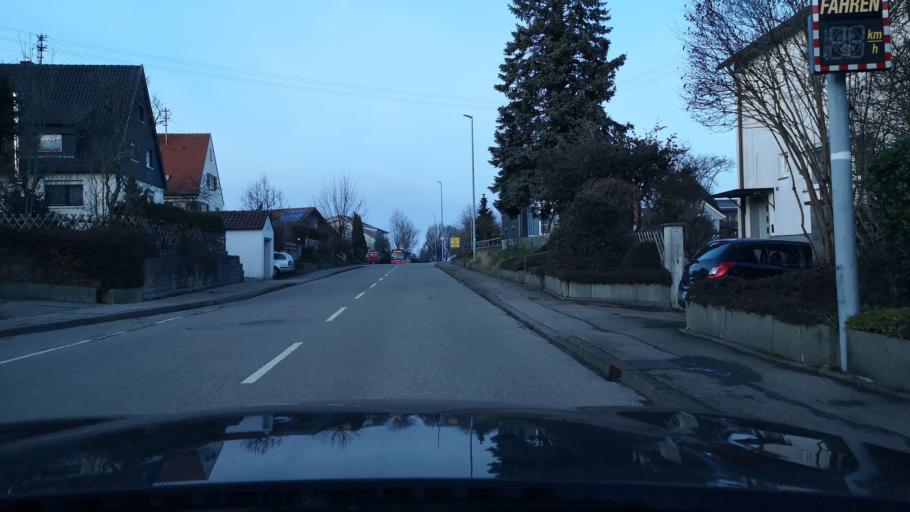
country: DE
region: Baden-Wuerttemberg
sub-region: Regierungsbezirk Stuttgart
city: Kaisersbach
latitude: 48.9311
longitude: 9.6390
